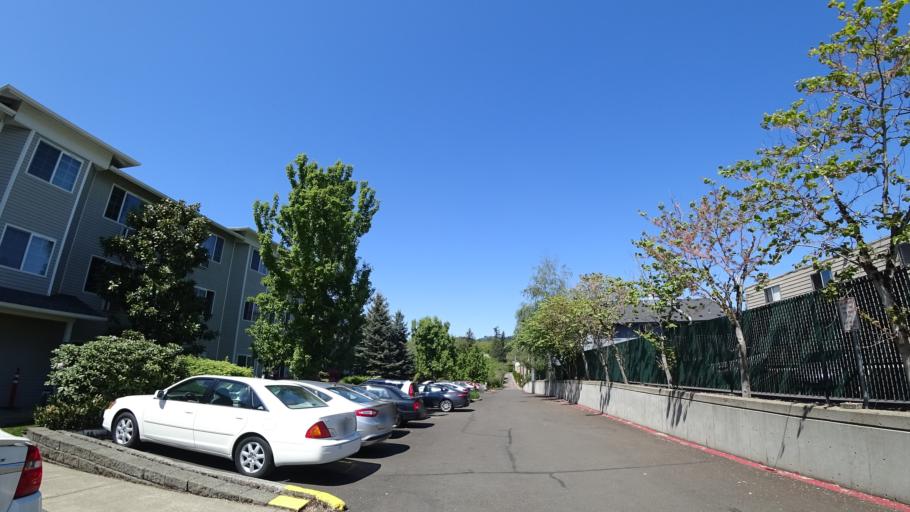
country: US
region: Oregon
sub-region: Washington County
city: Raleigh Hills
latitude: 45.4841
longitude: -122.7576
